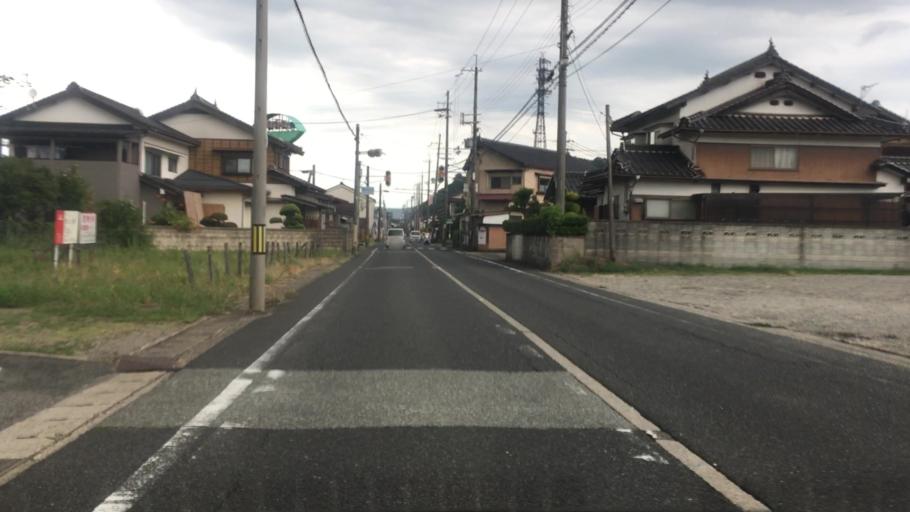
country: JP
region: Hyogo
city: Toyooka
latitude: 35.4720
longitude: 134.7813
